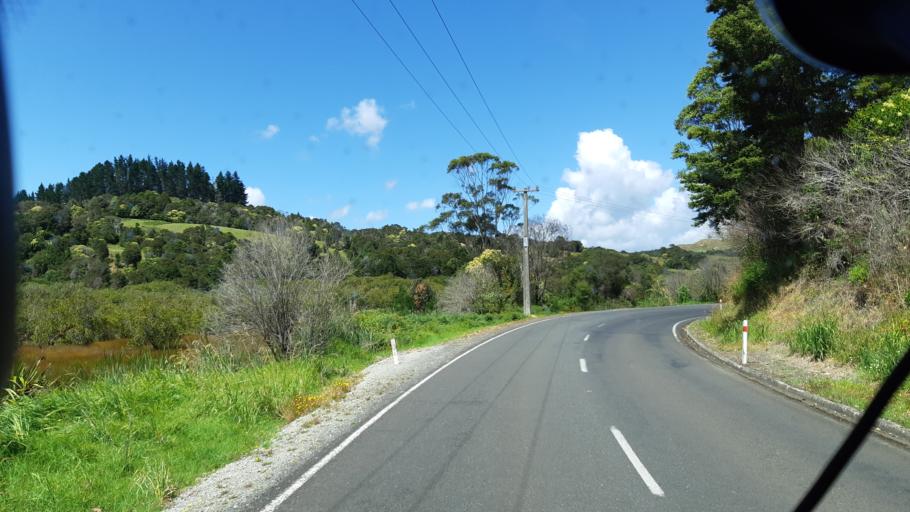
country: NZ
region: Northland
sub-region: Far North District
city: Taipa
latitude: -35.2748
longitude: 173.5210
